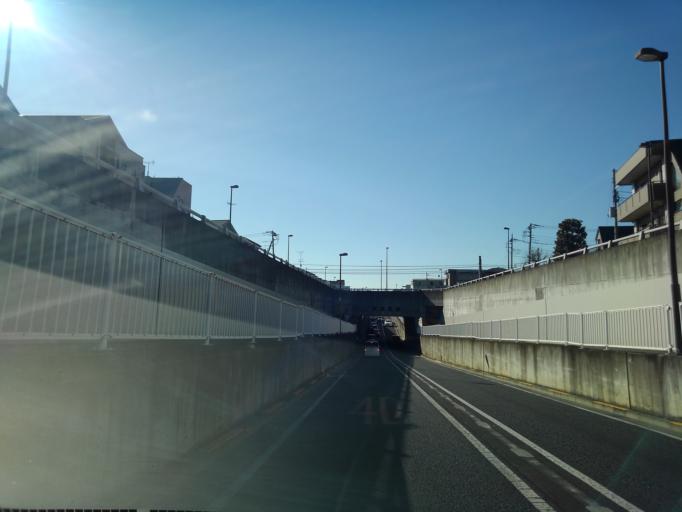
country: JP
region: Tokyo
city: Hino
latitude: 35.7091
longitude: 139.3784
